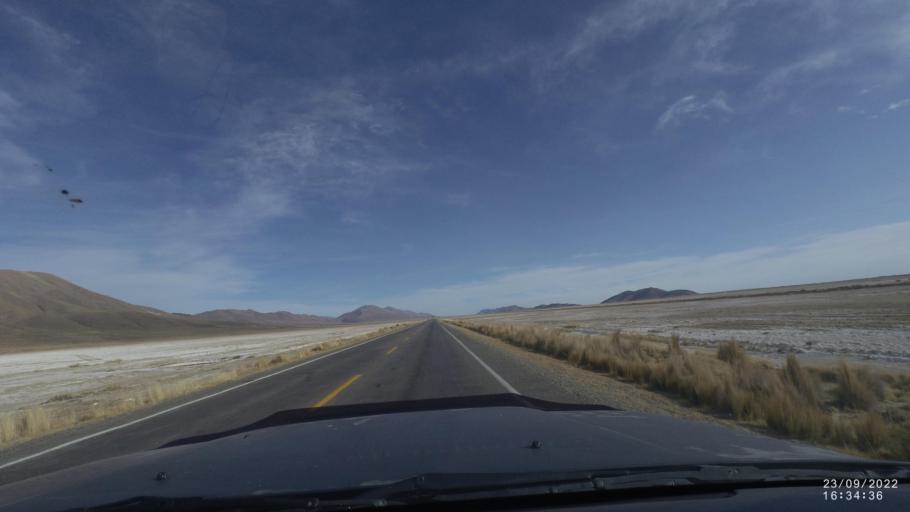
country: BO
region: Oruro
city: Machacamarca
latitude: -18.1915
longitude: -67.0138
